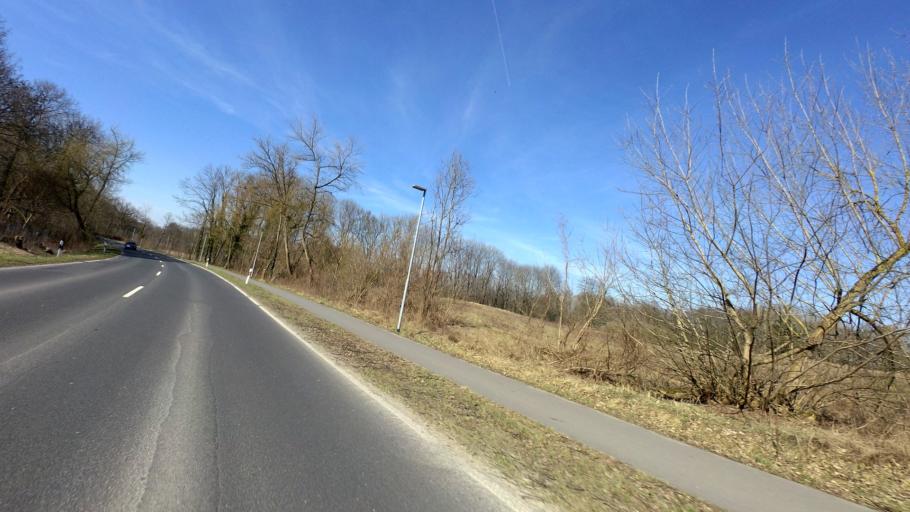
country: DE
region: Brandenburg
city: Muncheberg
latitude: 52.5203
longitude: 14.1080
